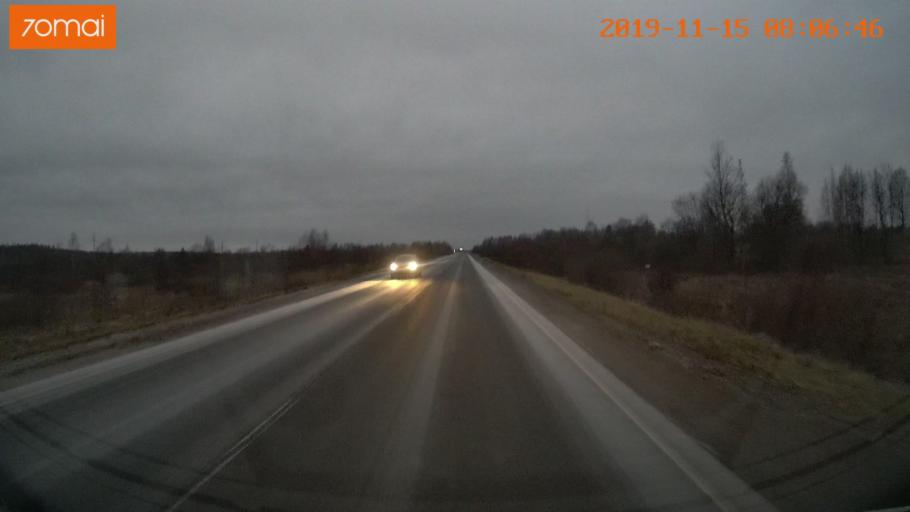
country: RU
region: Vologda
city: Cherepovets
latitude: 59.0235
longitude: 38.0316
